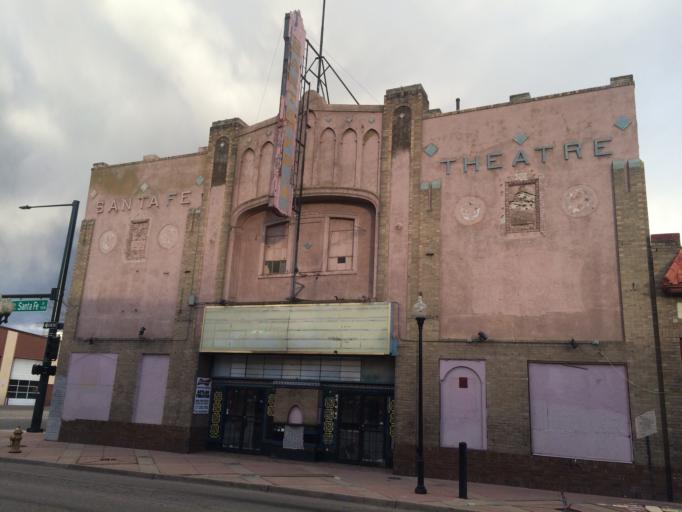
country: US
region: Colorado
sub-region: Denver County
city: Denver
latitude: 39.7318
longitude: -104.9987
